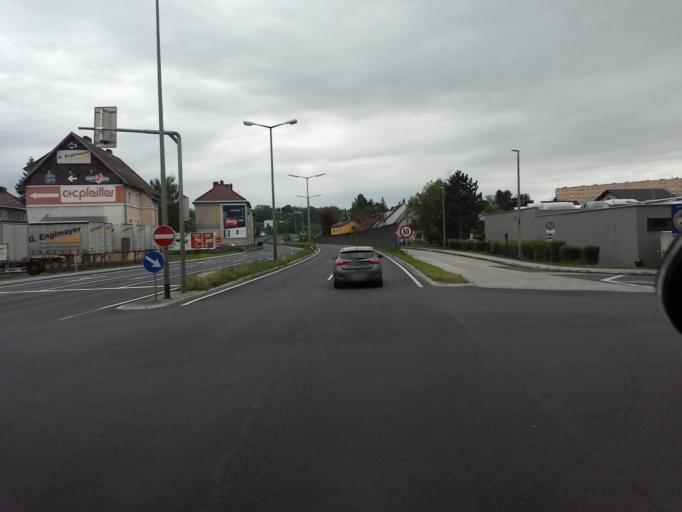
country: AT
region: Upper Austria
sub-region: Wels Stadt
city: Wels
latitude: 48.1629
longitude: 14.0413
